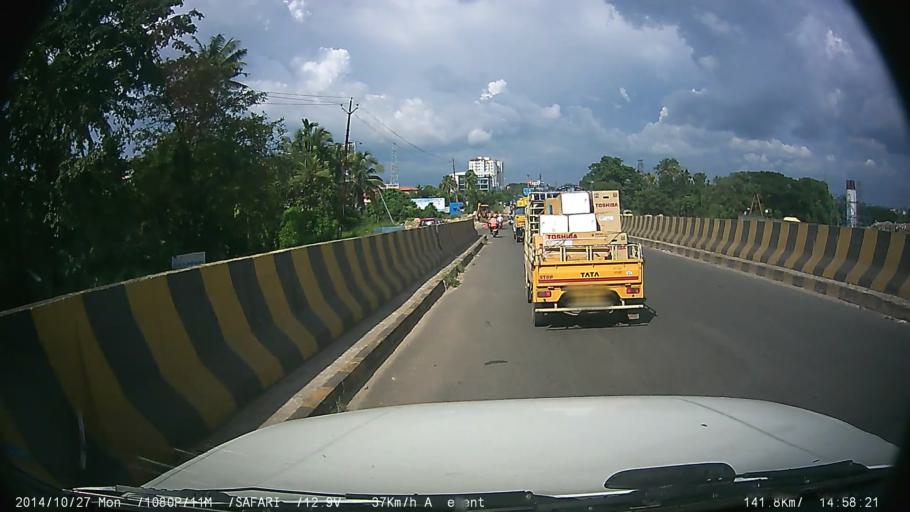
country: IN
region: Kerala
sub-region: Ernakulam
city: Elur
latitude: 10.0650
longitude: 76.3269
